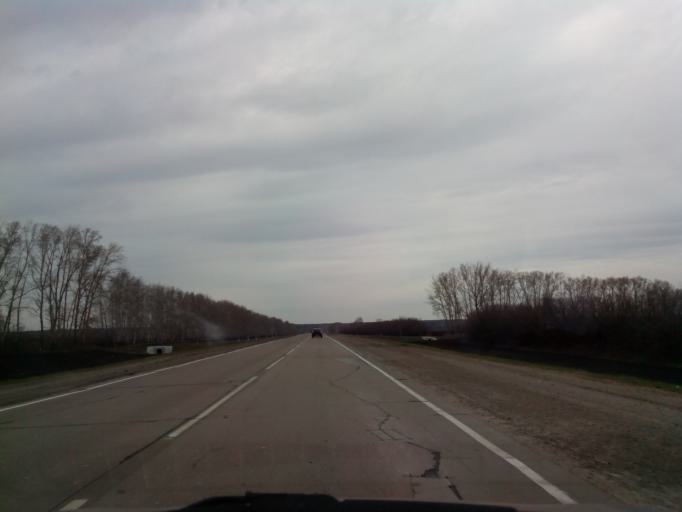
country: RU
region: Tambov
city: Znamenka
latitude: 52.5044
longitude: 41.3641
